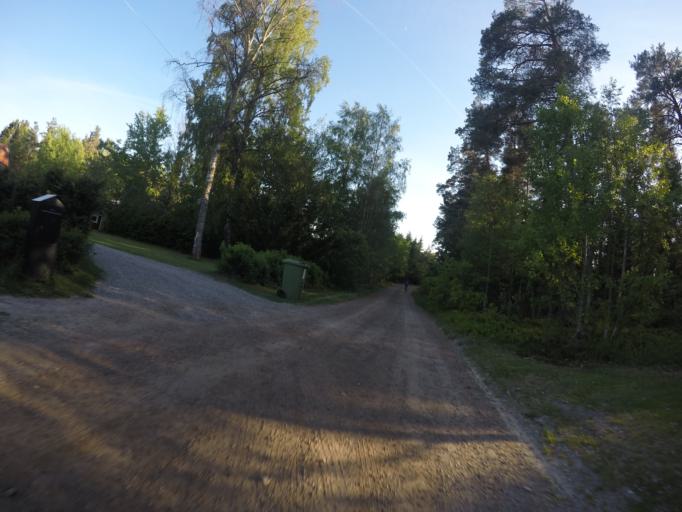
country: SE
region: Soedermanland
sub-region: Eskilstuna Kommun
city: Eskilstuna
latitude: 59.3460
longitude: 16.5302
